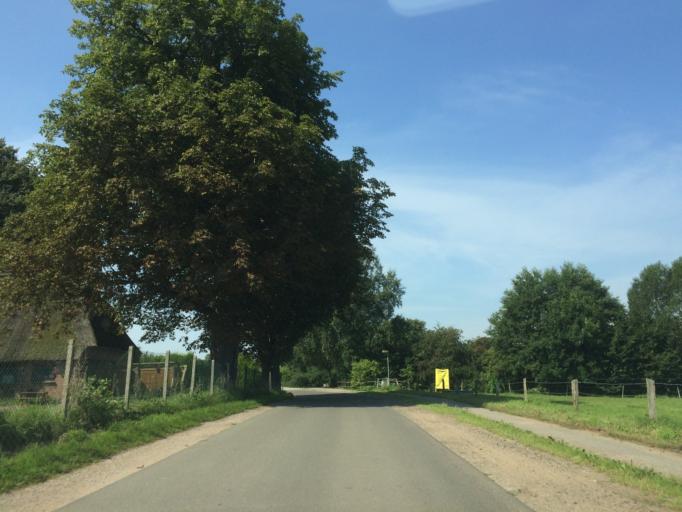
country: DE
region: Schleswig-Holstein
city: Lindau
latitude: 54.4205
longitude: 9.9087
